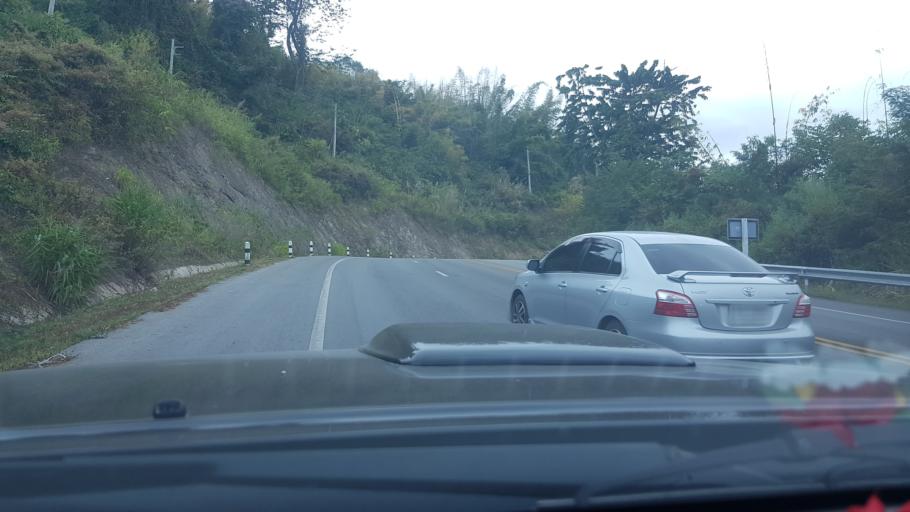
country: TH
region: Phetchabun
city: Khao Kho
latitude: 16.5510
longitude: 101.0321
